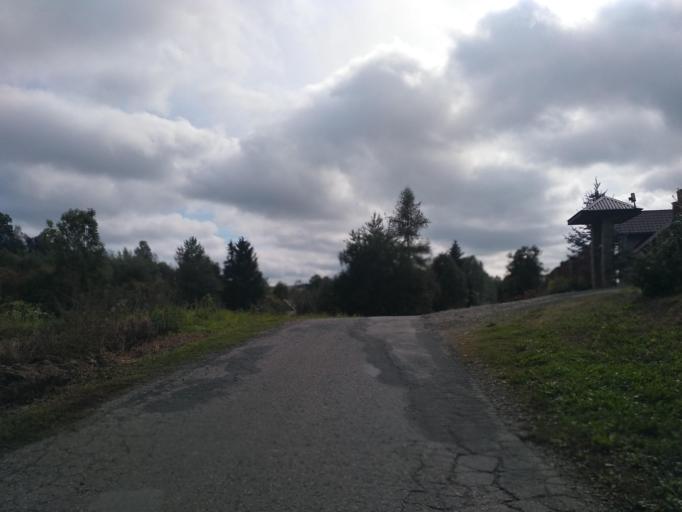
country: PL
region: Subcarpathian Voivodeship
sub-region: Powiat ropczycko-sedziszowski
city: Niedzwiada
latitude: 49.9366
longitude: 21.4680
